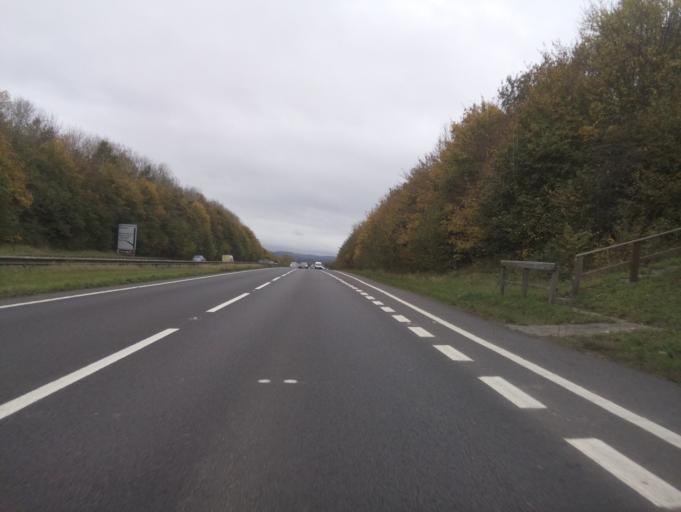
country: GB
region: England
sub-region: Somerset
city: Stoke-sub-Hamdon
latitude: 50.9555
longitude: -2.7642
